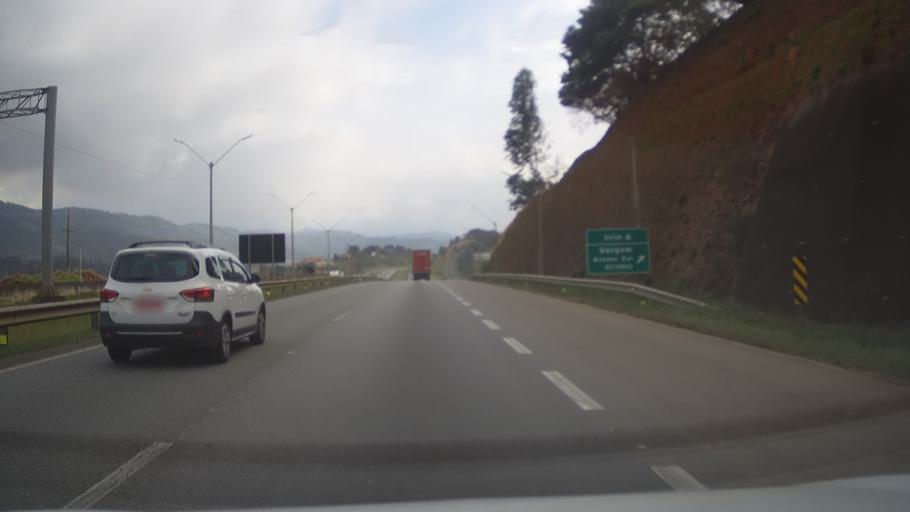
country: BR
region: Minas Gerais
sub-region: Extrema
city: Extrema
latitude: -22.9014
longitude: -46.4205
